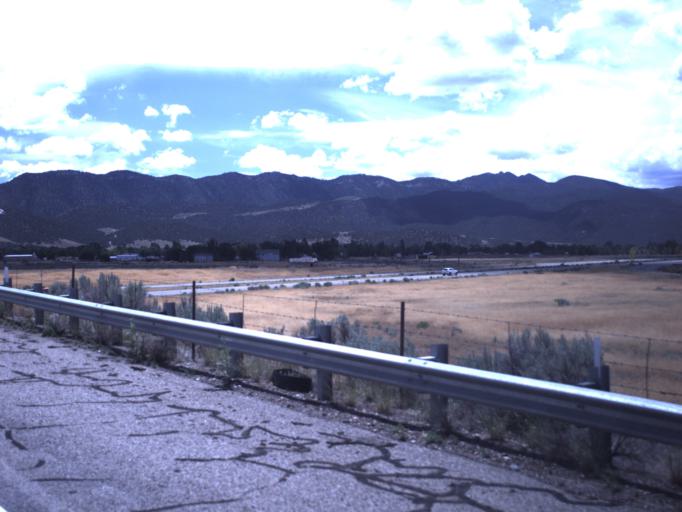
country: US
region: Utah
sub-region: Iron County
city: Parowan
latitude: 37.8594
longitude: -112.8293
